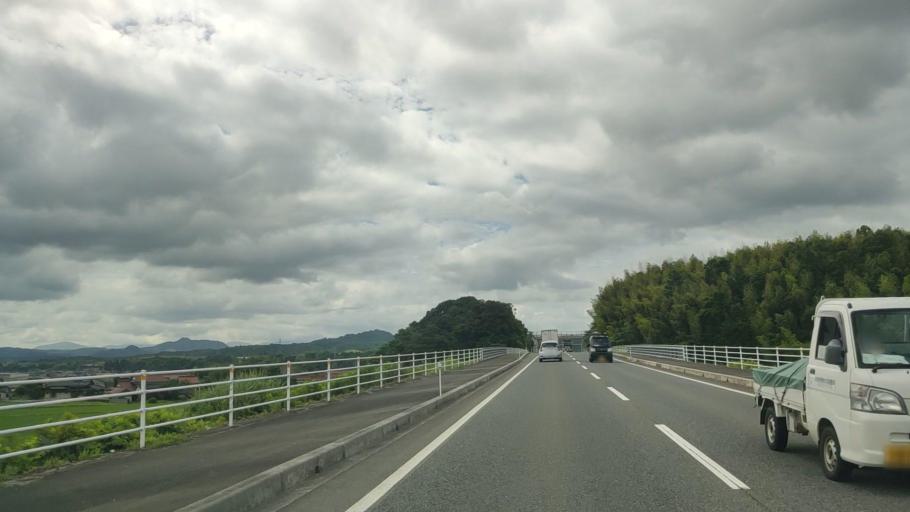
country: JP
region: Tottori
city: Yonago
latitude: 35.3939
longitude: 133.3819
